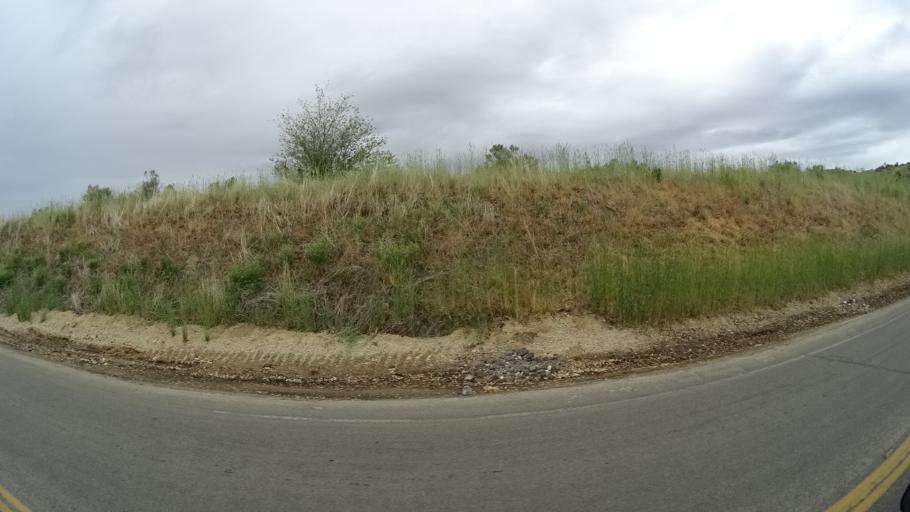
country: US
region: Idaho
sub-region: Ada County
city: Boise
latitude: 43.6149
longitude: -116.1840
